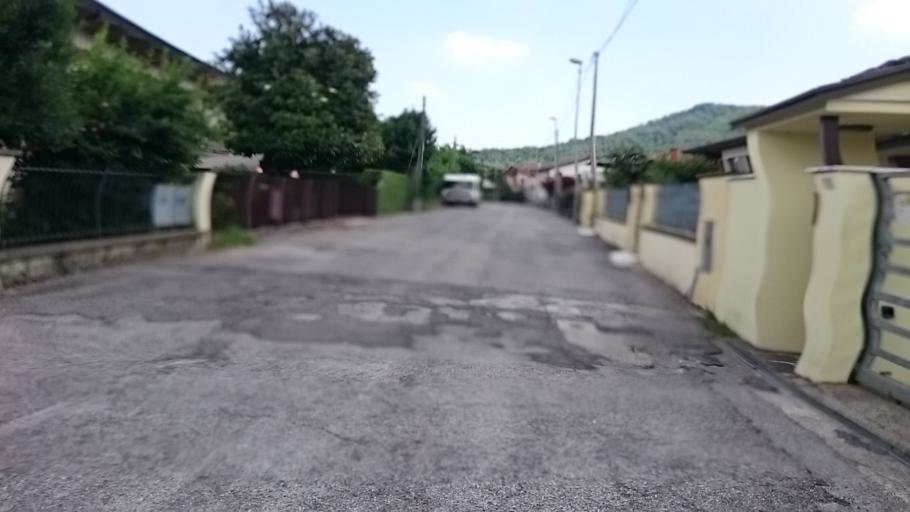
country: IT
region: Veneto
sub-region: Provincia di Padova
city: Torreglia
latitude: 45.3318
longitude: 11.7577
